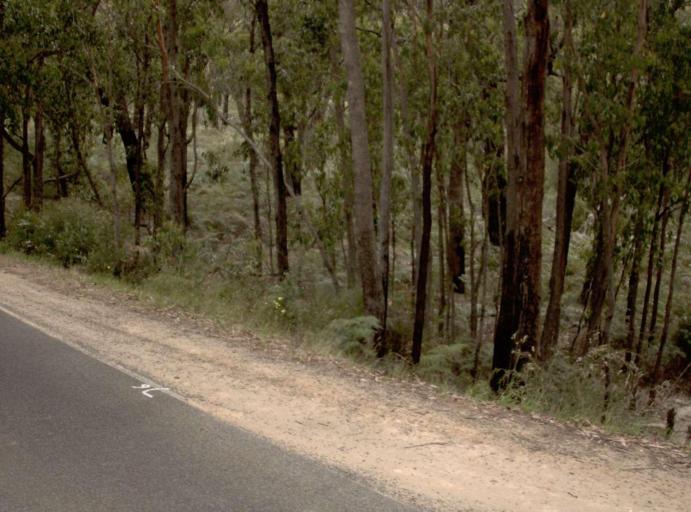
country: AU
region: Victoria
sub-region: Latrobe
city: Traralgon
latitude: -38.4144
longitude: 146.8165
